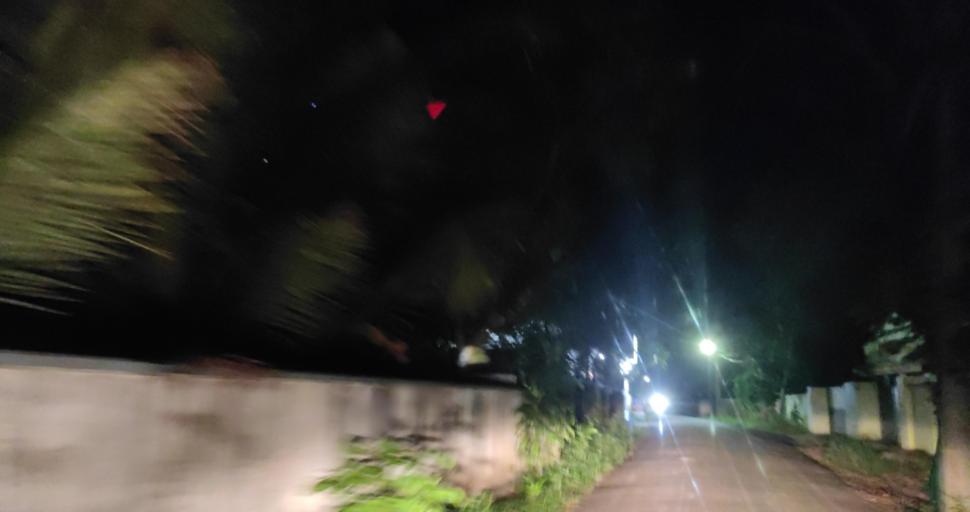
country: IN
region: Kerala
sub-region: Alappuzha
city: Shertallai
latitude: 9.6201
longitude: 76.3346
